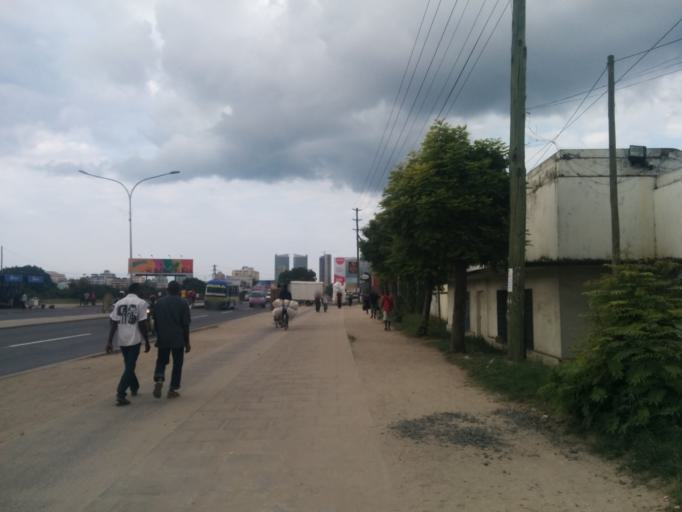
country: TZ
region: Dar es Salaam
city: Dar es Salaam
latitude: -6.8307
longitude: 39.2712
